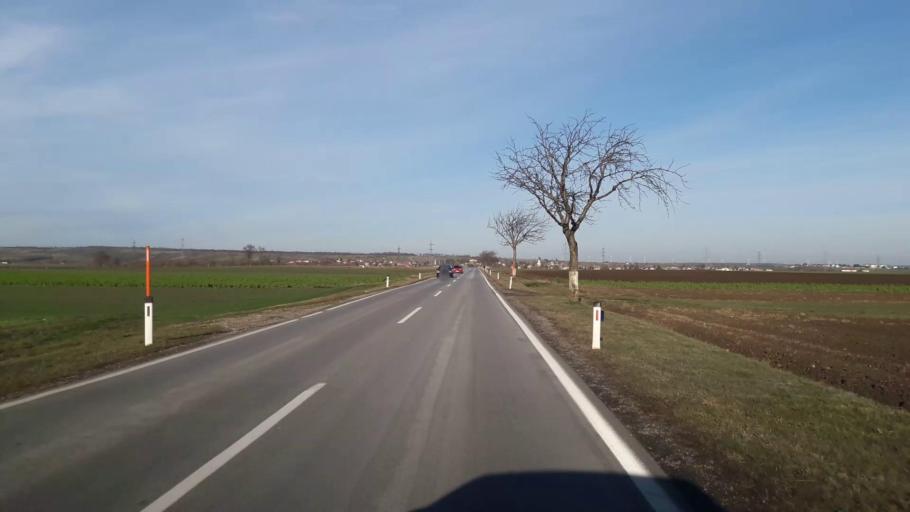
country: AT
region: Lower Austria
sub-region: Politischer Bezirk Mistelbach
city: Bockfliess
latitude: 48.3383
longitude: 16.5938
